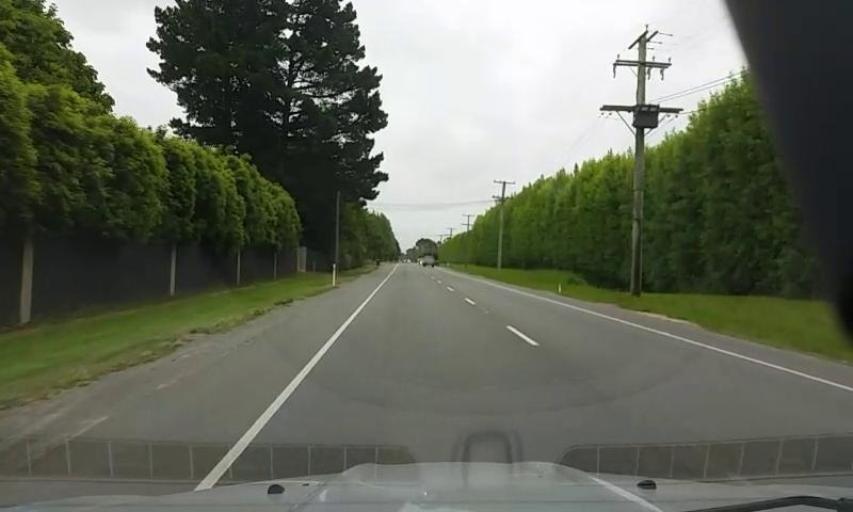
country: NZ
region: Canterbury
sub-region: Selwyn District
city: Prebbleton
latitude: -43.5165
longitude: 172.5216
